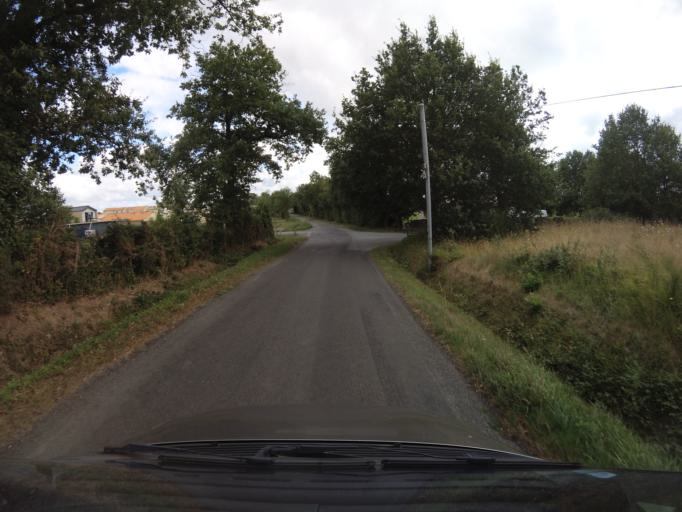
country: FR
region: Pays de la Loire
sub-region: Departement de la Vendee
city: Saint-Philbert-de-Bouaine
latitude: 46.9961
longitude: -1.5249
